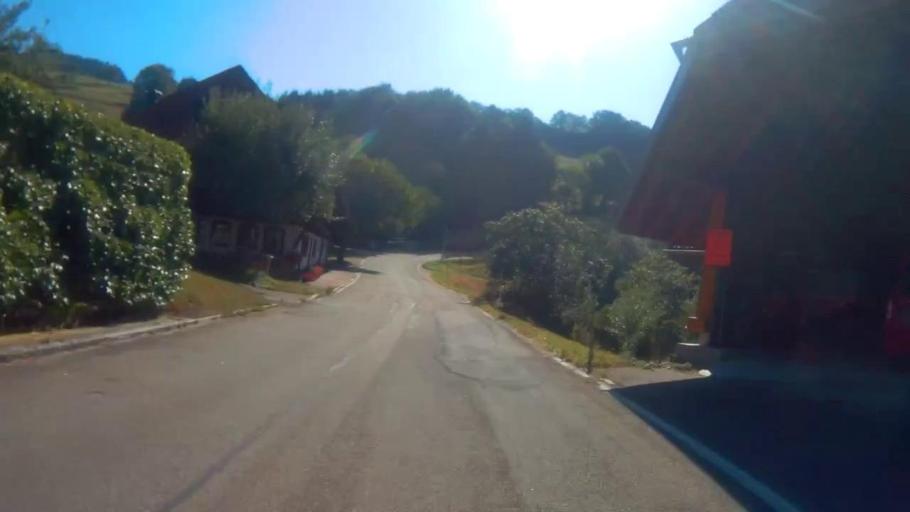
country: DE
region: Baden-Wuerttemberg
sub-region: Freiburg Region
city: Wembach
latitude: 47.7636
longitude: 7.8966
